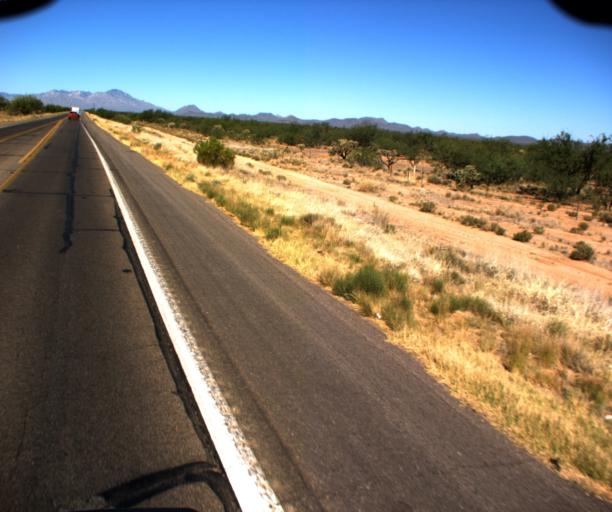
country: US
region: Arizona
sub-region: Pima County
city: Three Points
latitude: 32.1102
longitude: -111.2296
